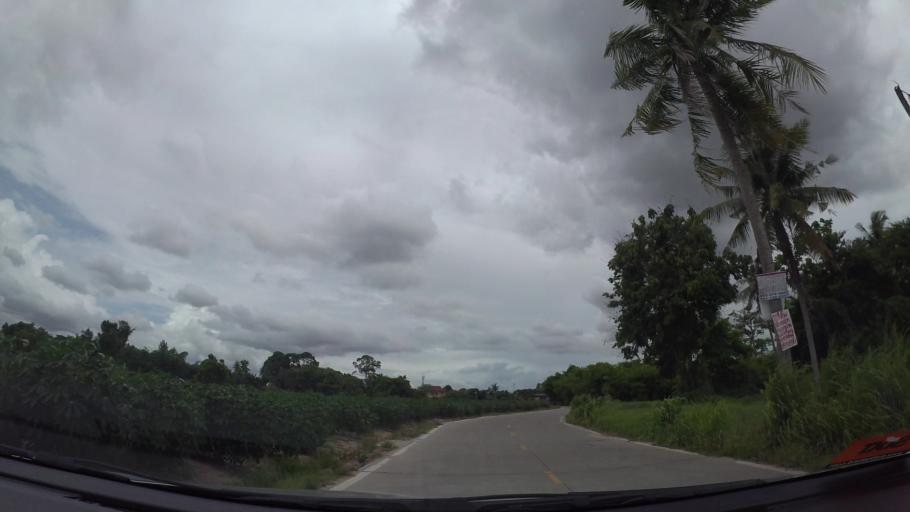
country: TH
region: Chon Buri
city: Si Racha
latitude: 13.1692
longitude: 100.9711
